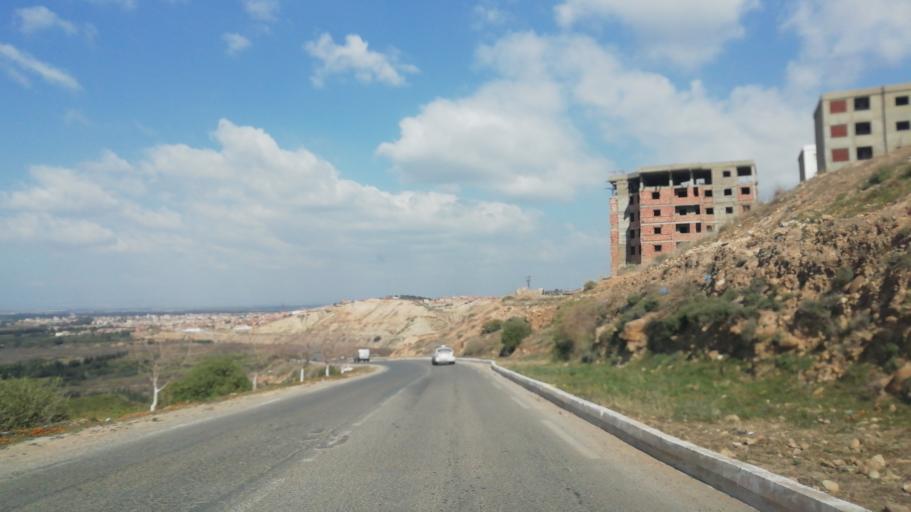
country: DZ
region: Mascara
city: Mascara
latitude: 35.5572
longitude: 0.0672
